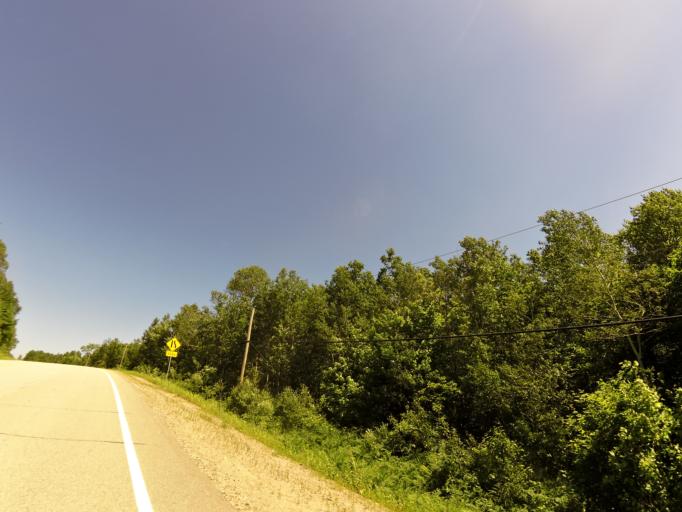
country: CA
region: Quebec
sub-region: Abitibi-Temiscamingue
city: Temiscaming
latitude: 46.7566
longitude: -79.0768
